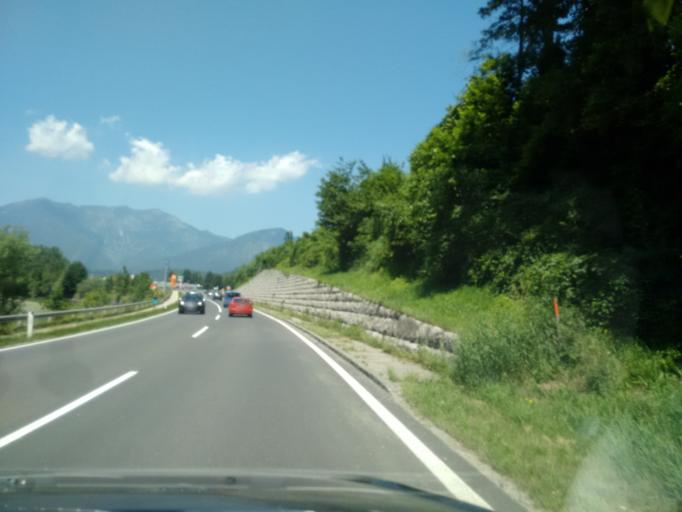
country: AT
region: Upper Austria
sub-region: Politischer Bezirk Gmunden
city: Bad Ischl
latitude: 47.6879
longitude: 13.6259
